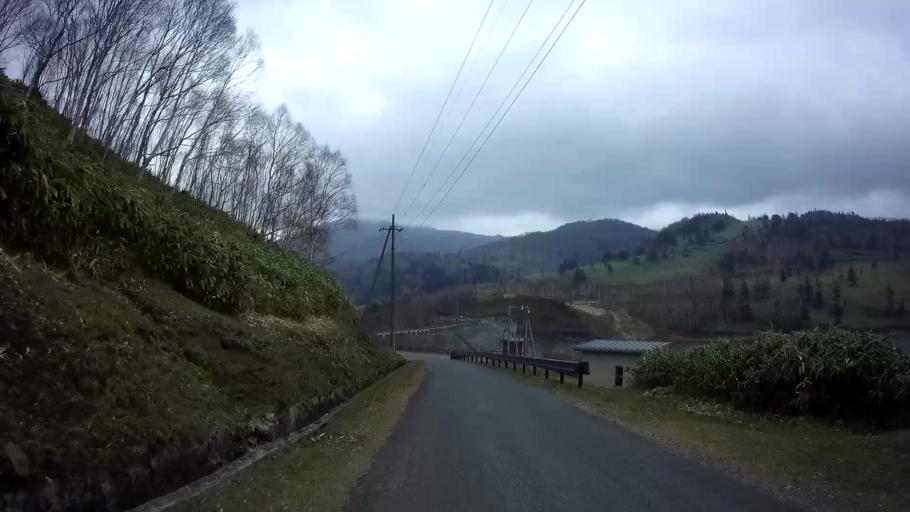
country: JP
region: Gunma
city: Nakanojomachi
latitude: 36.7177
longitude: 138.6405
